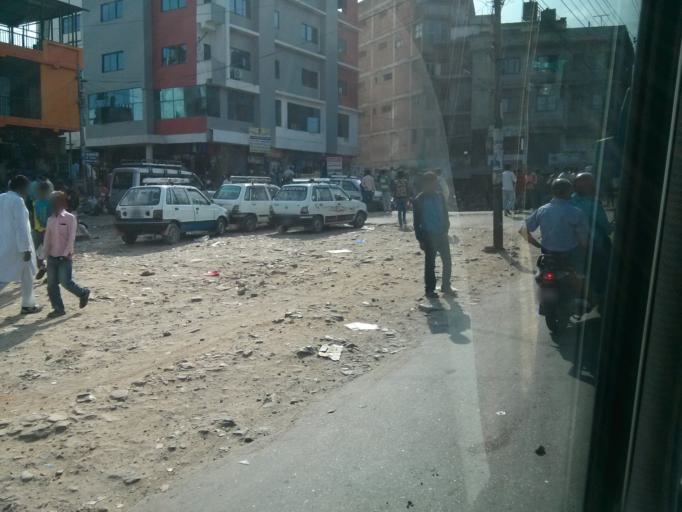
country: NP
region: Central Region
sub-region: Bagmati Zone
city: Kathmandu
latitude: 27.7067
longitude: 85.3447
